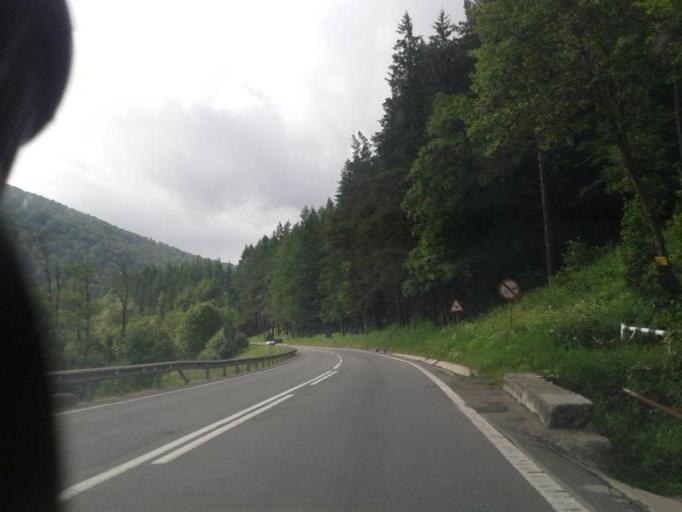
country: RO
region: Prahova
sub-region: Oras Azuga
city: Azuga
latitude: 45.4637
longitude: 25.5641
